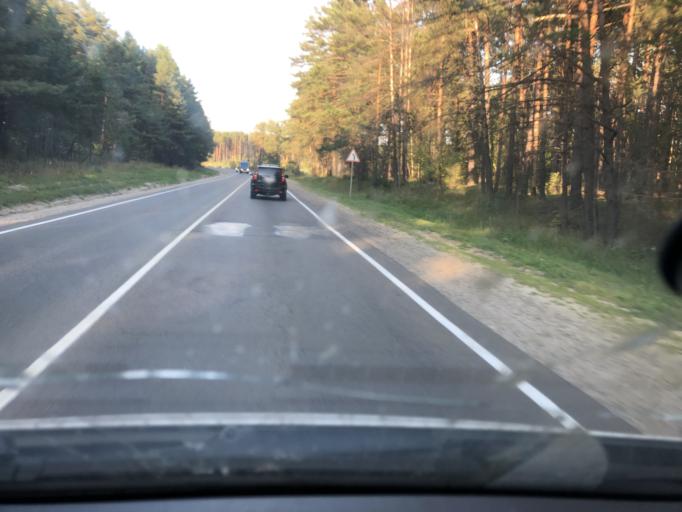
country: RU
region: Kaluga
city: Peremyshl'
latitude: 54.3528
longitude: 36.1987
